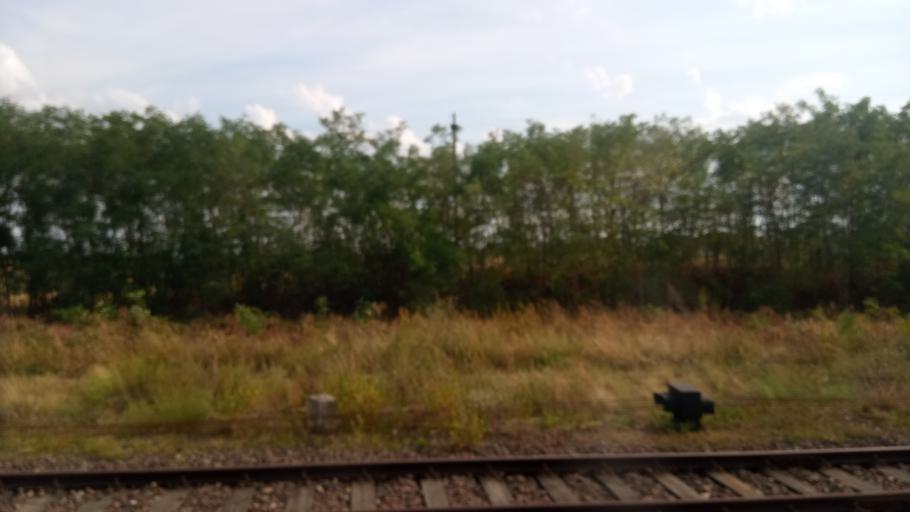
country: PL
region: Greater Poland Voivodeship
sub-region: Powiat pilski
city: Osiek nad Notecia
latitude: 53.1197
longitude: 17.3044
